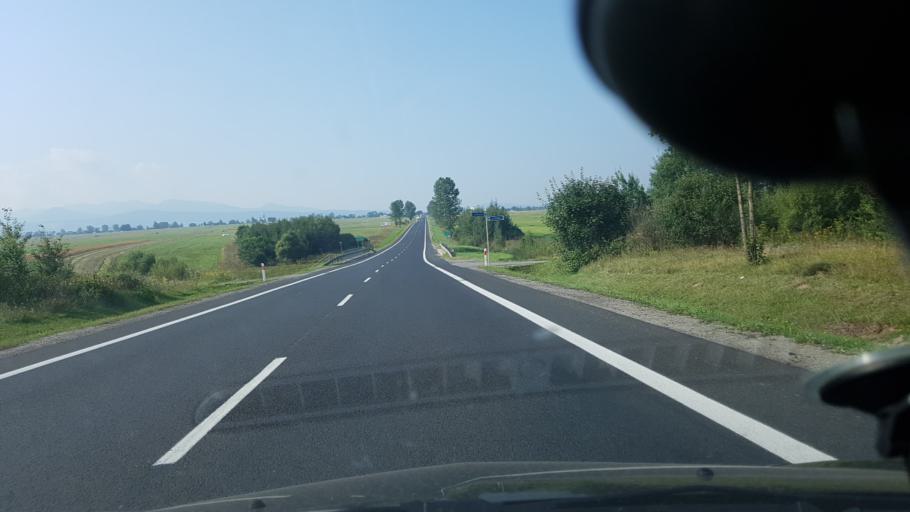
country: PL
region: Lesser Poland Voivodeship
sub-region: Powiat nowotarski
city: Chyzne
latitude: 49.4423
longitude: 19.6829
